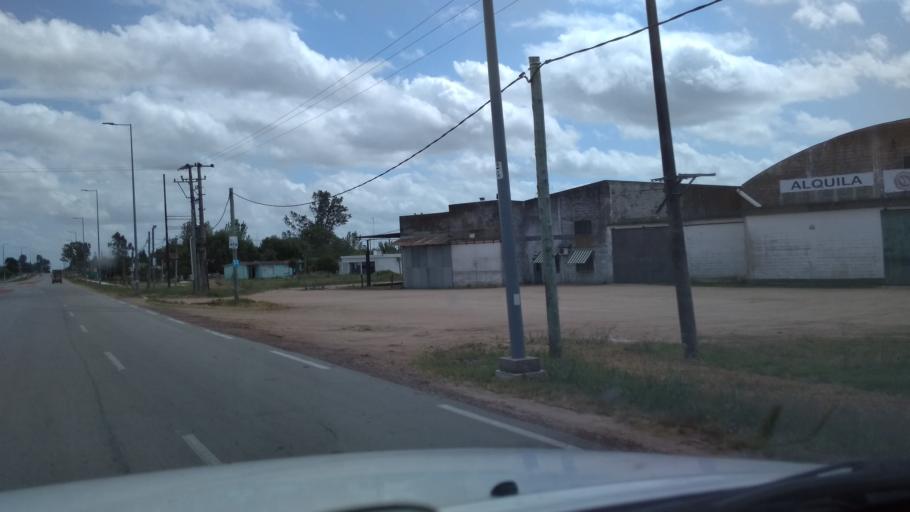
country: UY
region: Canelones
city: San Bautista
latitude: -34.4385
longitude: -55.9642
